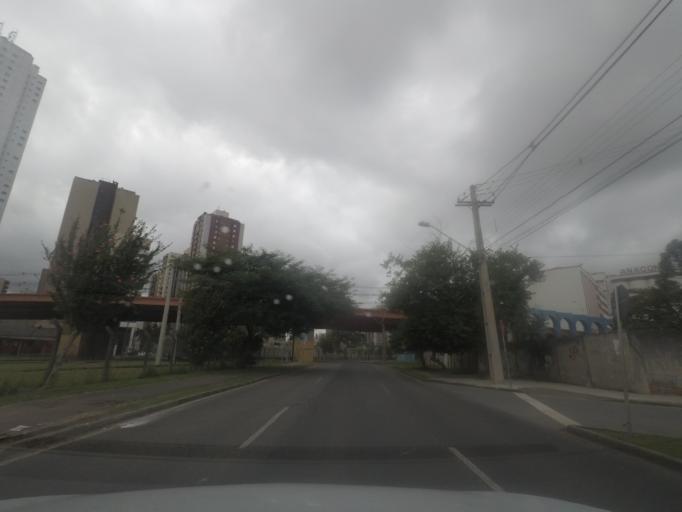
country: BR
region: Parana
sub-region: Curitiba
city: Curitiba
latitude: -25.4366
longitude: -49.2540
